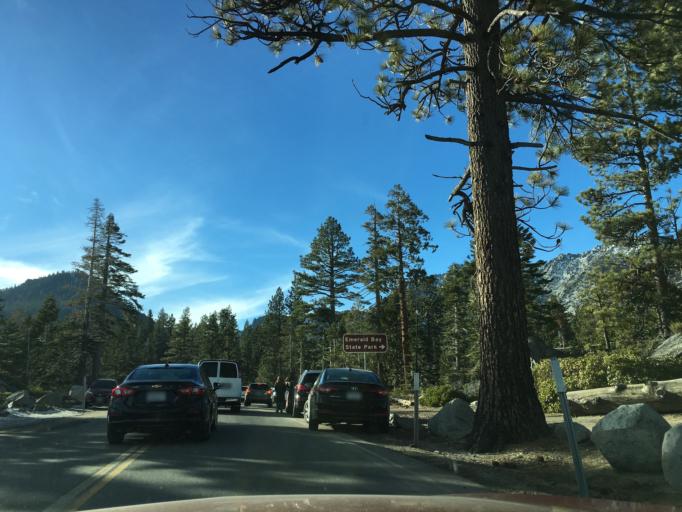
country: US
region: California
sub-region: El Dorado County
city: South Lake Tahoe
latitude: 38.9515
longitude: -120.0845
